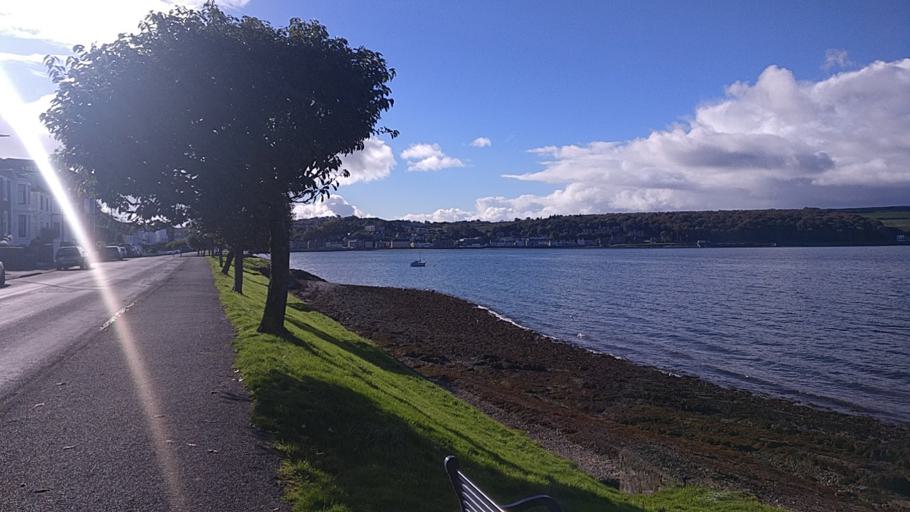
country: GB
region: Scotland
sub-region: Argyll and Bute
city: Rothesay
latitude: 55.8434
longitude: -5.0404
